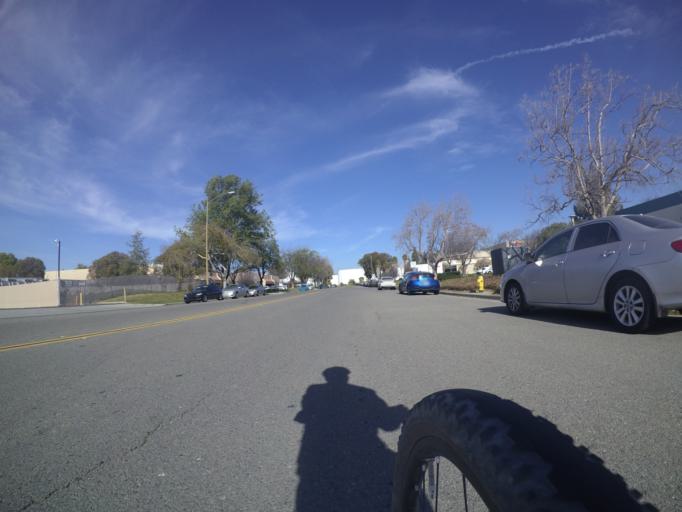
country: US
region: California
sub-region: Santa Clara County
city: Milpitas
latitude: 37.3877
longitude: -121.9138
